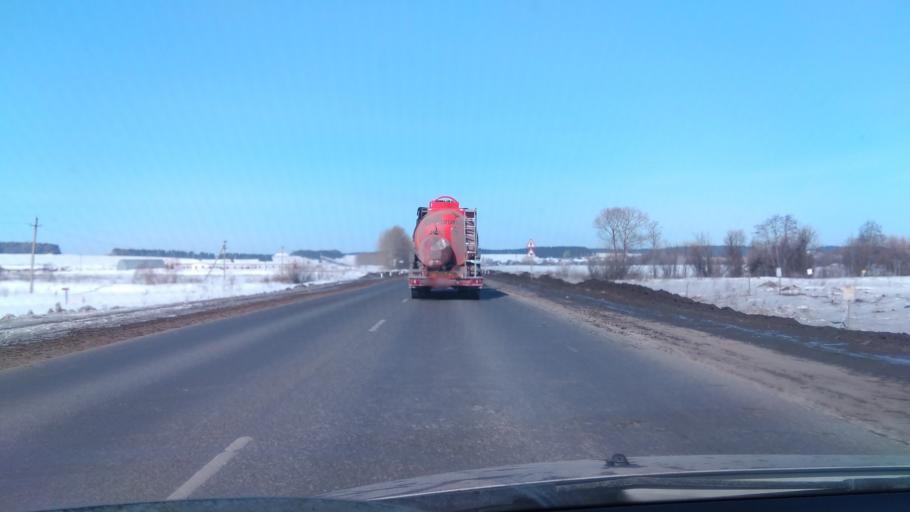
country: RU
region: Perm
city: Kukushtan
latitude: 57.5082
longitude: 56.6472
